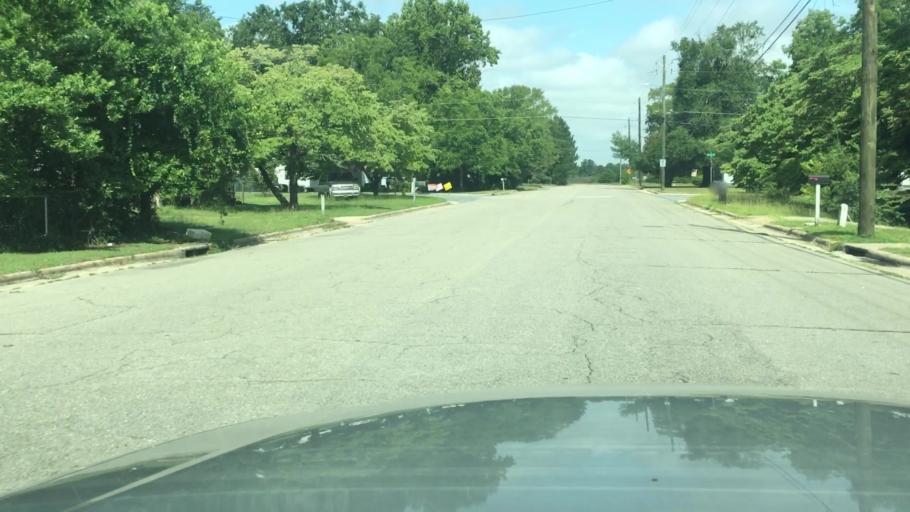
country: US
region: North Carolina
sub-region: Cumberland County
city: Fayetteville
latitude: 35.0247
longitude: -78.9014
